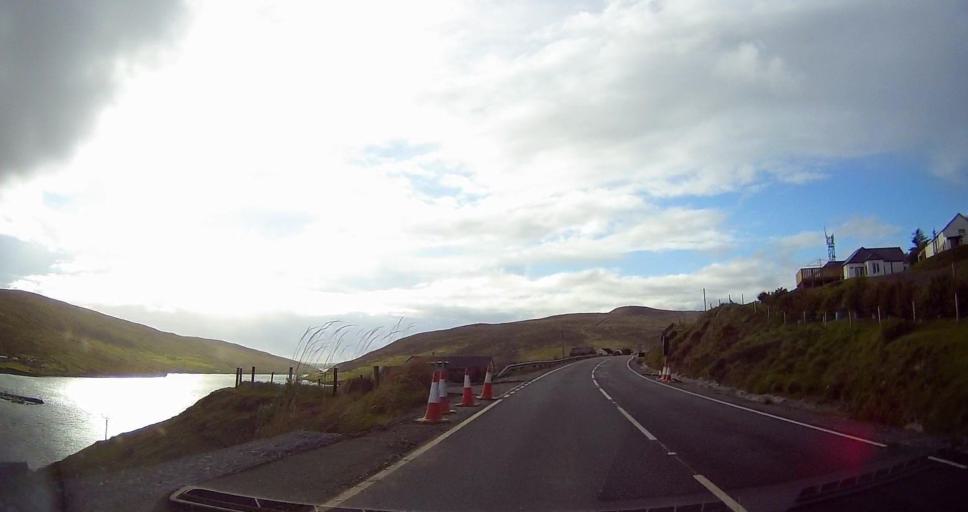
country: GB
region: Scotland
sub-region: Shetland Islands
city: Lerwick
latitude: 60.3515
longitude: -1.2588
